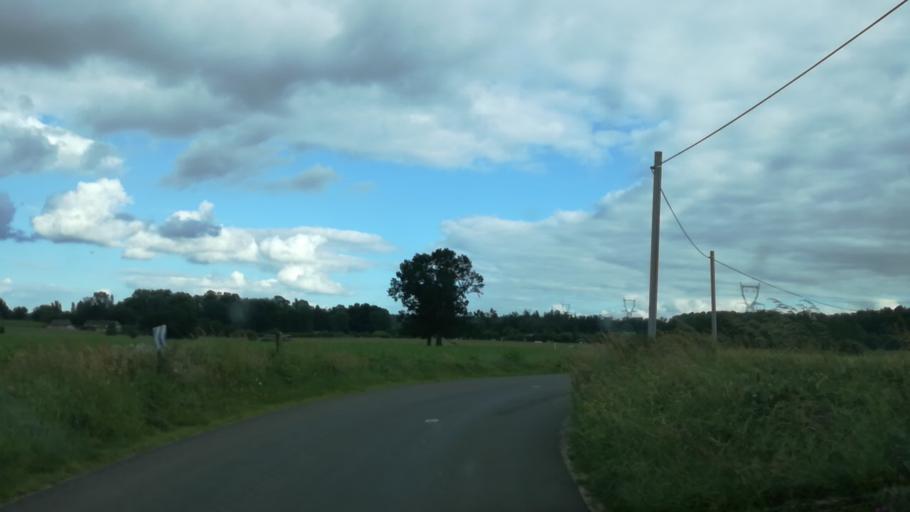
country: FR
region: Haute-Normandie
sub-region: Departement de l'Eure
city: Bourgtheroulde-Infreville
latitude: 49.2742
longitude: 0.8129
